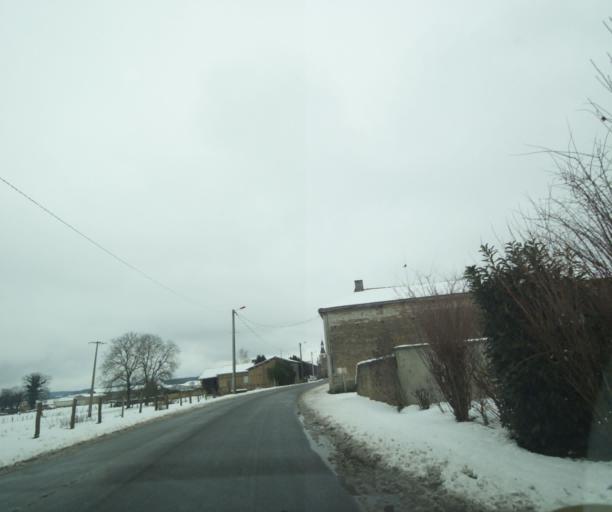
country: FR
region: Champagne-Ardenne
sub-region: Departement de la Haute-Marne
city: Montier-en-Der
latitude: 48.4226
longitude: 4.8188
